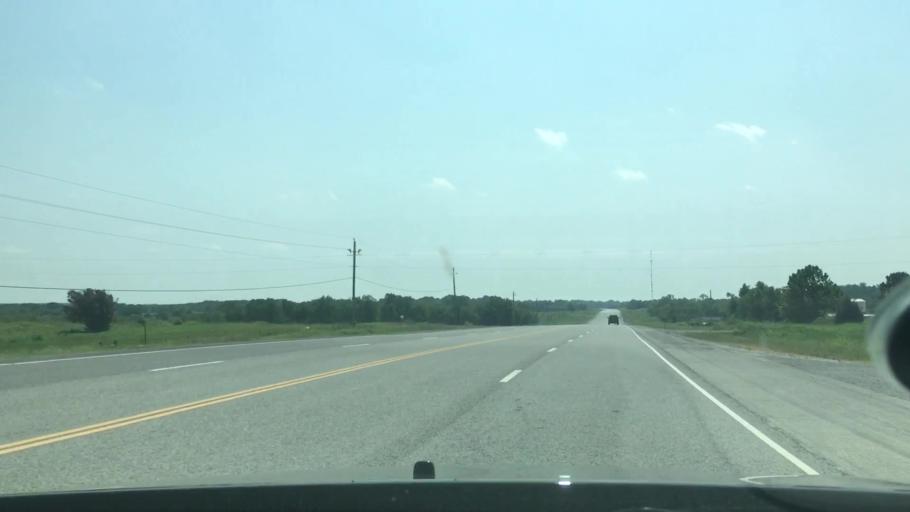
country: US
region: Oklahoma
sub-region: Atoka County
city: Atoka
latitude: 34.3694
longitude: -96.1050
